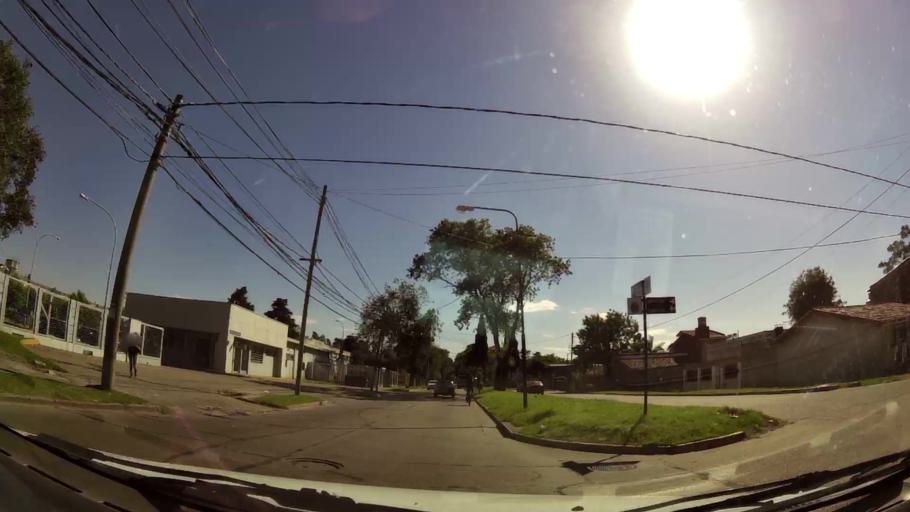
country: AR
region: Buenos Aires
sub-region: Partido de San Isidro
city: San Isidro
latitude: -34.4743
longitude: -58.5412
